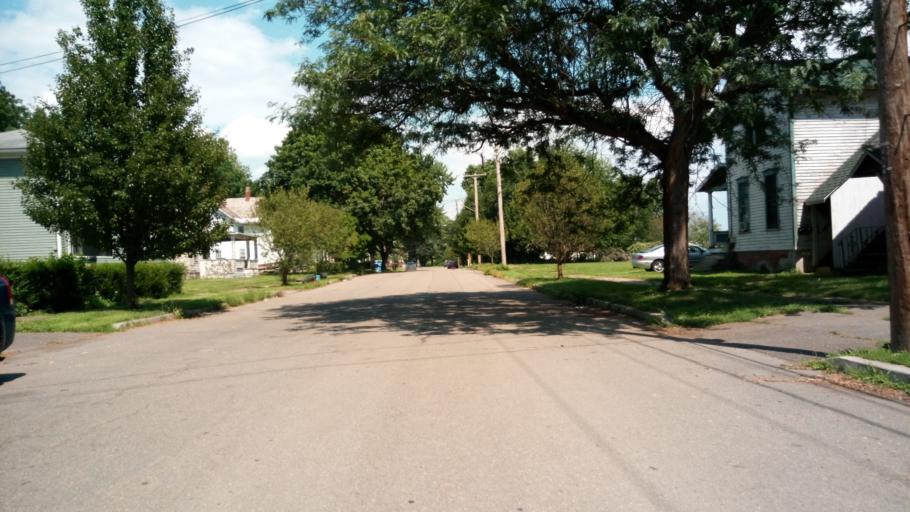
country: US
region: New York
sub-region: Chemung County
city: Elmira
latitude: 42.0829
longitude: -76.8212
